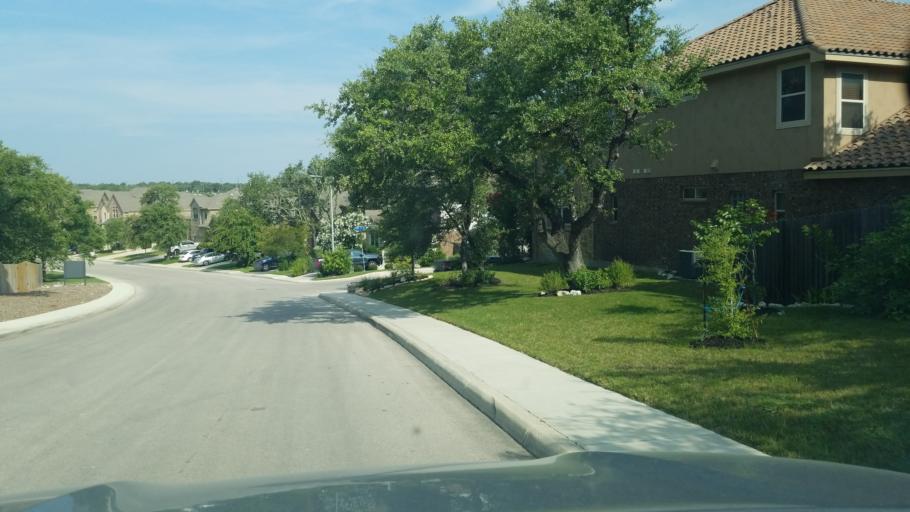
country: US
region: Texas
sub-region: Bexar County
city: Scenic Oaks
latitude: 29.7148
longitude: -98.6563
